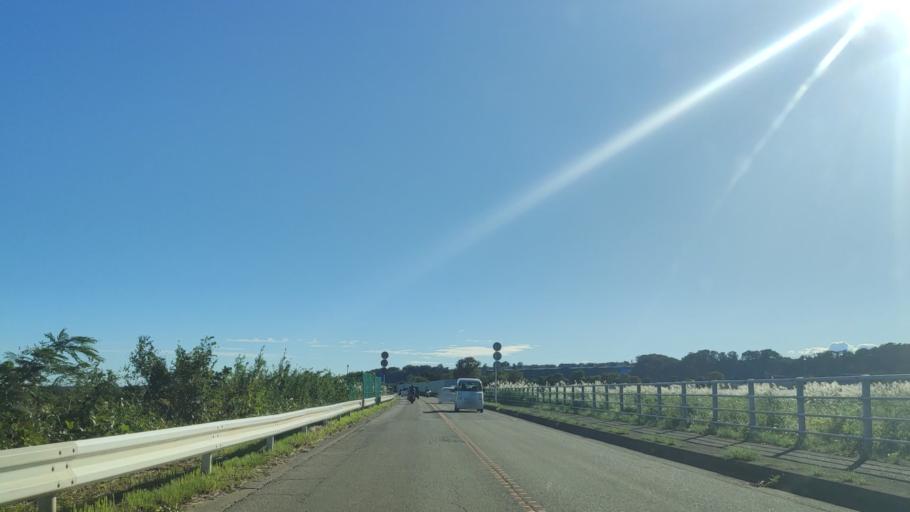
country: JP
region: Kanagawa
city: Zama
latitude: 35.5059
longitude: 139.3734
